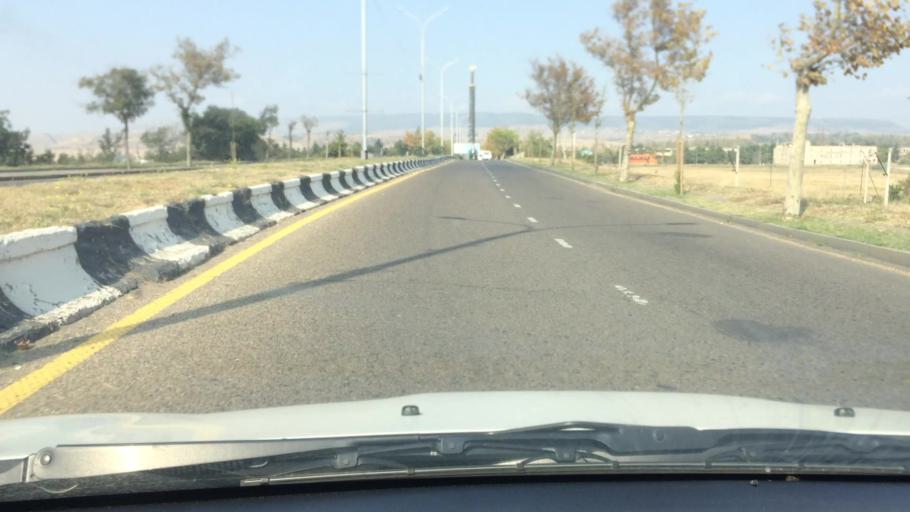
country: GE
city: Didi Lilo
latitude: 41.6855
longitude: 44.9534
